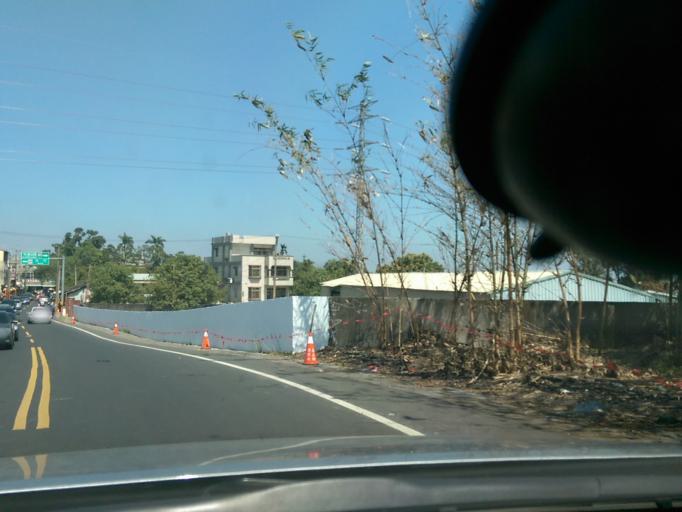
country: TW
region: Taiwan
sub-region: Chiayi
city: Jiayi Shi
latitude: 23.4243
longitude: 120.4493
